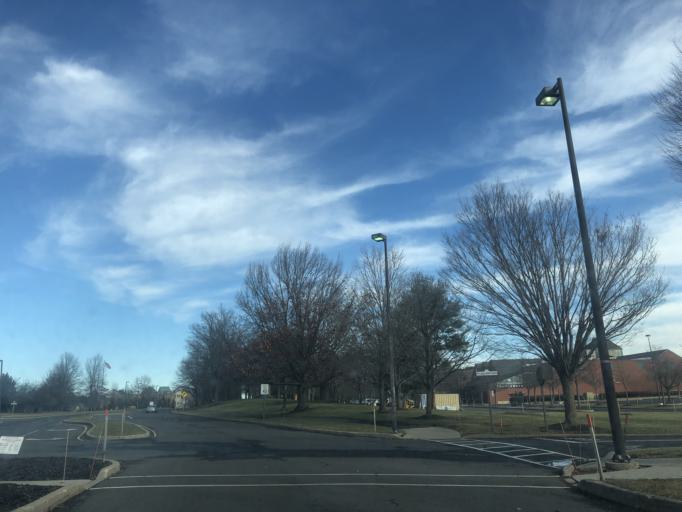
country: US
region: New Jersey
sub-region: Somerset County
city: Kingston
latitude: 40.3542
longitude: -74.6157
